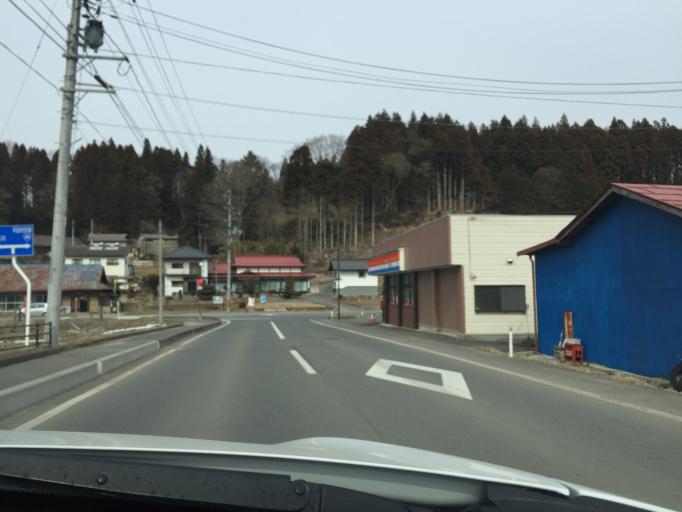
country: JP
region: Fukushima
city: Ishikawa
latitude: 37.2149
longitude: 140.5665
